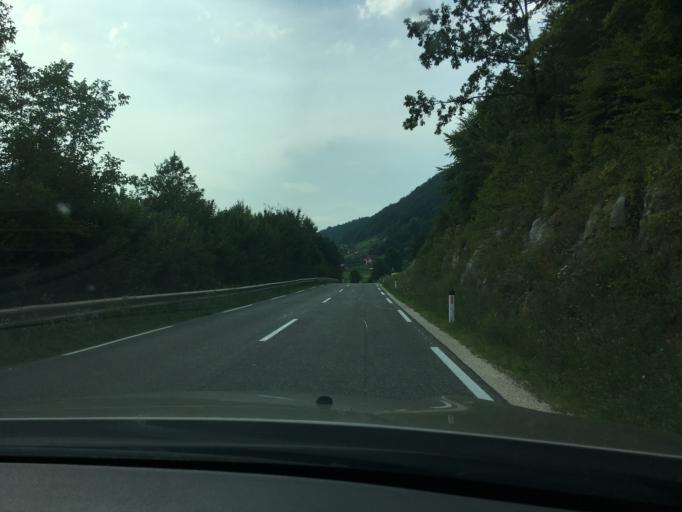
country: SI
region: Zuzemberk
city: Zuzemberk
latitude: 45.7929
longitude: 14.9876
